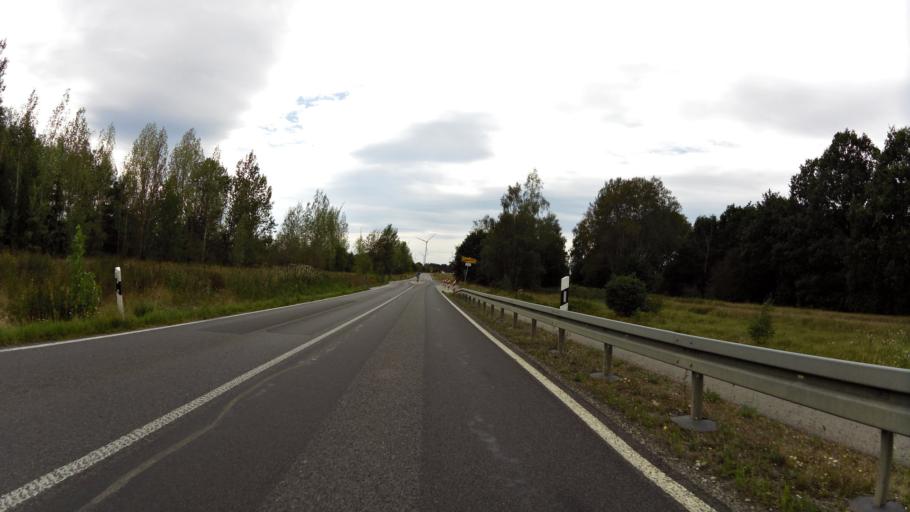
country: DE
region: Brandenburg
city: Heinersbruck
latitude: 51.8035
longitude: 14.4884
